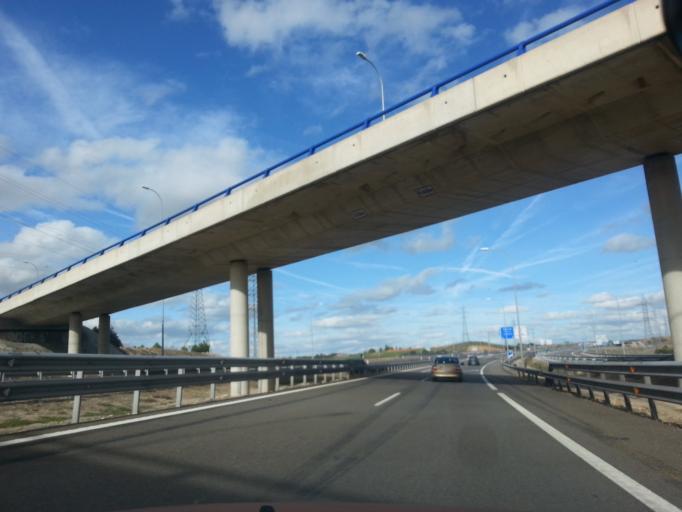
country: ES
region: Castille and Leon
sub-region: Provincia de Salamanca
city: Villamayor
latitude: 40.9960
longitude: -5.6748
